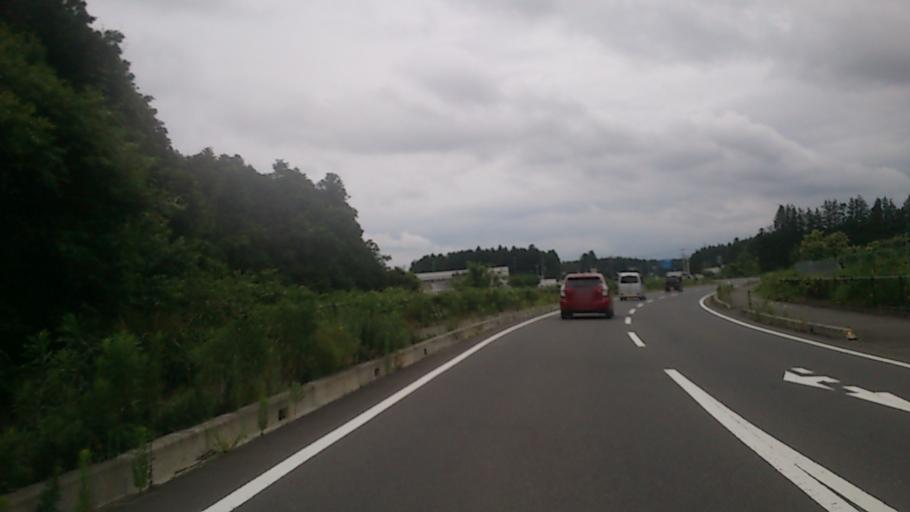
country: JP
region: Ibaraki
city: Ishioka
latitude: 36.2336
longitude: 140.3248
